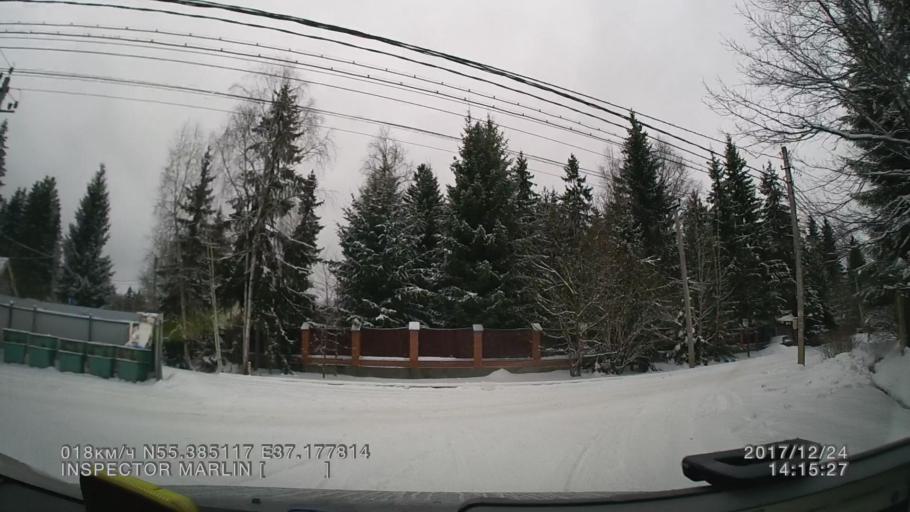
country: RU
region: Moskovskaya
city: Troitsk
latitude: 55.3851
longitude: 37.1778
